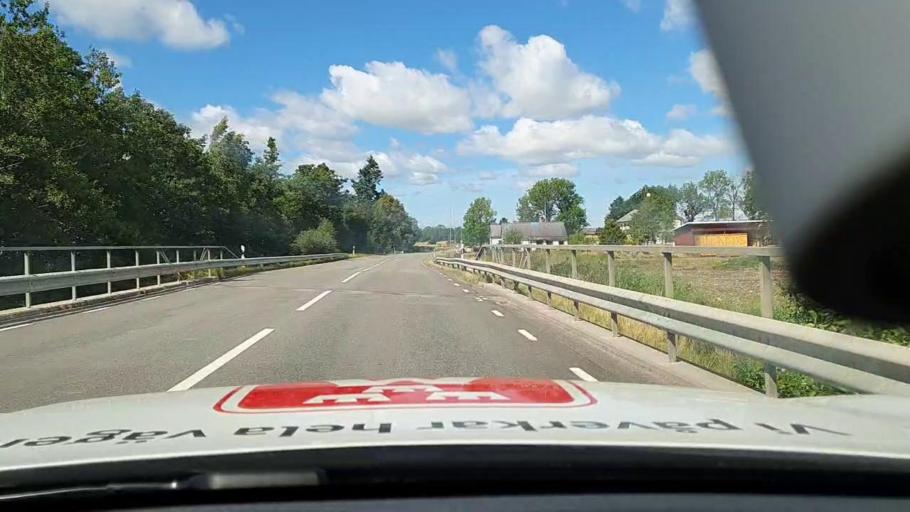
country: SE
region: Vaestra Goetaland
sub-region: Toreboda Kommun
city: Toereboda
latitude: 58.5762
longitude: 14.0962
